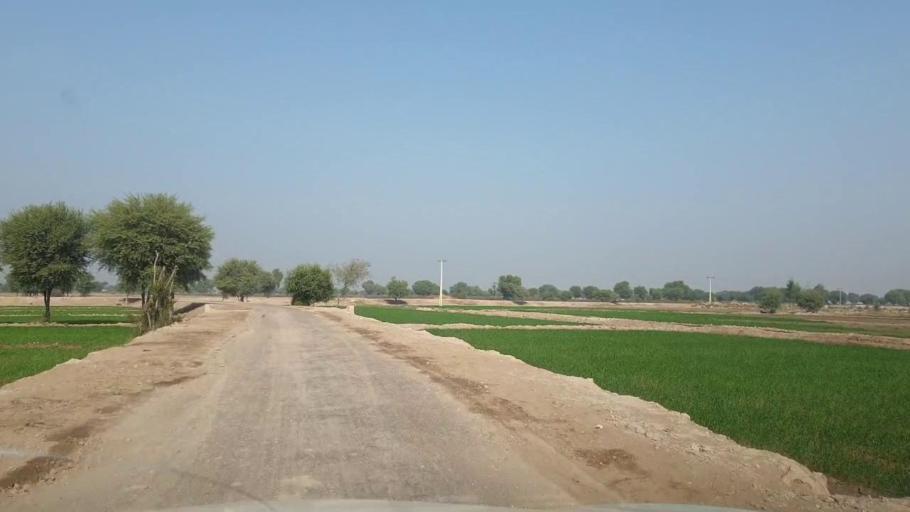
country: PK
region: Sindh
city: Bhan
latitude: 26.5101
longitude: 67.7962
